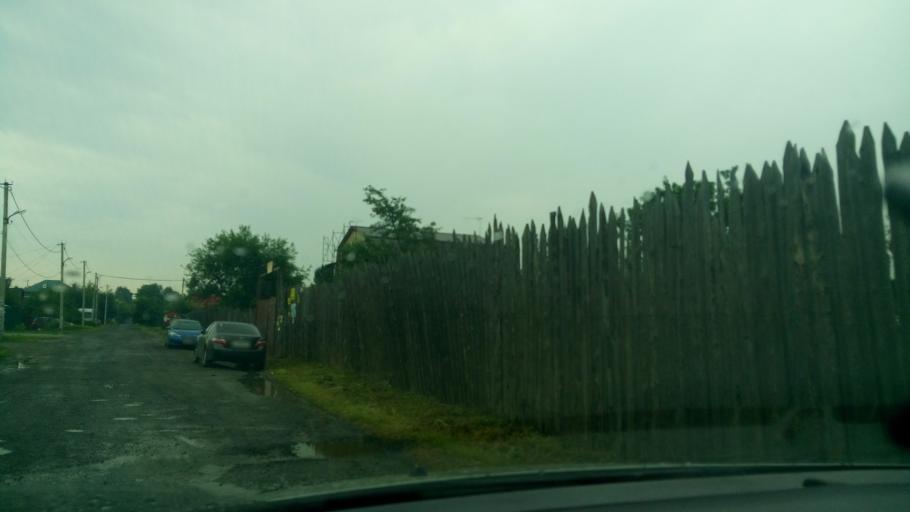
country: RU
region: Sverdlovsk
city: Yekaterinburg
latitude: 56.8890
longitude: 60.5621
